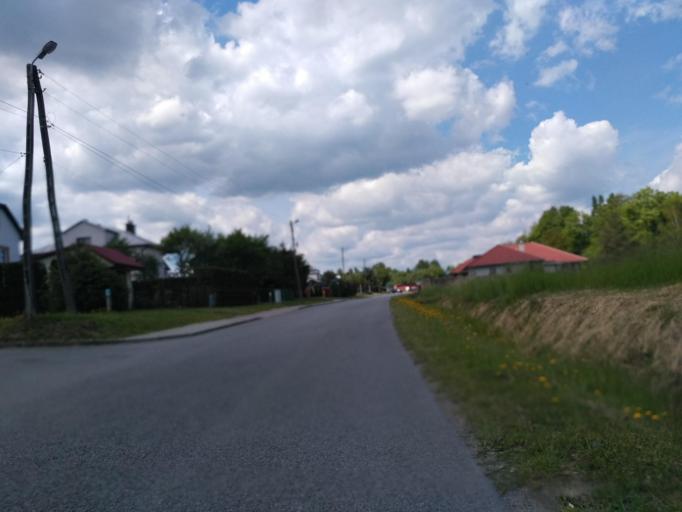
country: PL
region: Subcarpathian Voivodeship
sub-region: Powiat krosnienski
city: Dukla
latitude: 49.5550
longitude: 21.6747
